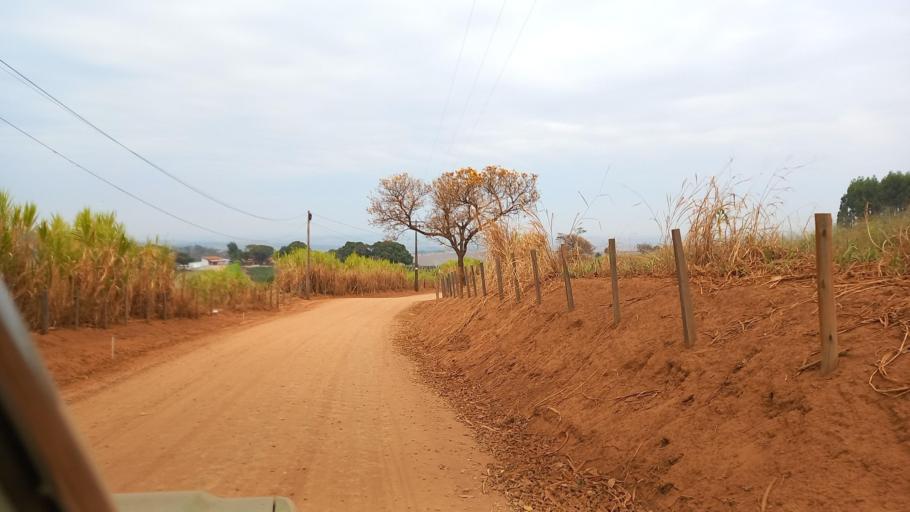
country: BR
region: Sao Paulo
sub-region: Moji-Guacu
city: Mogi-Gaucu
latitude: -22.3278
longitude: -46.8578
